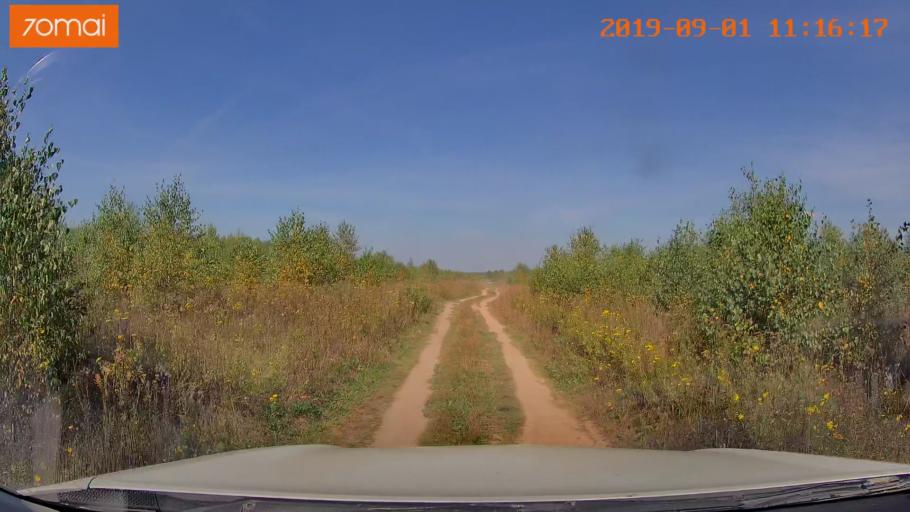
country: RU
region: Kaluga
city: Detchino
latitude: 54.8235
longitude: 36.3685
